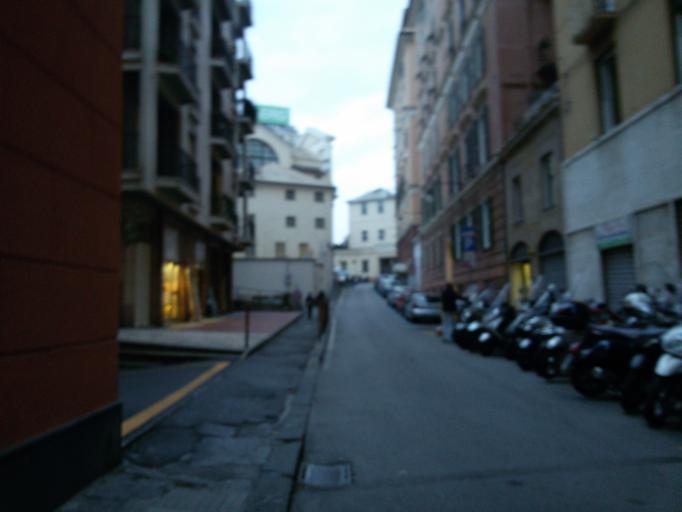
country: IT
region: Liguria
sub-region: Provincia di Genova
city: San Teodoro
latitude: 44.4031
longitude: 8.9384
